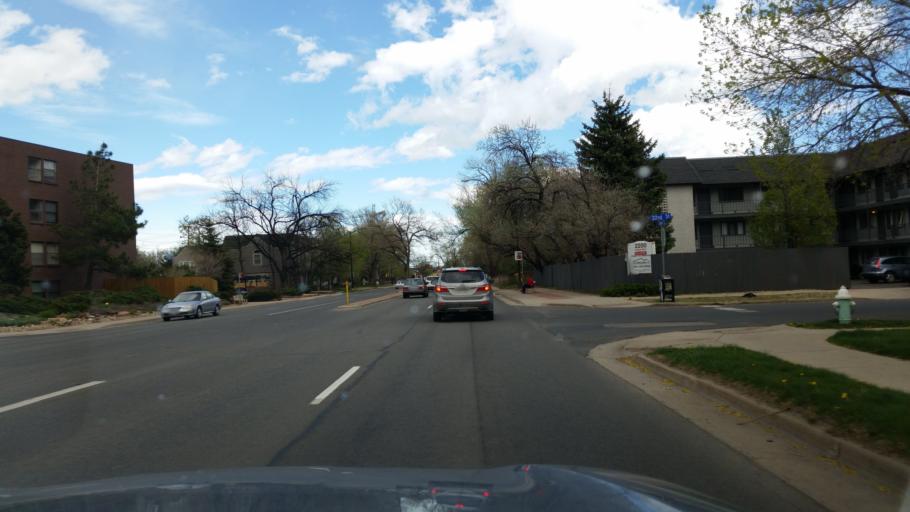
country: US
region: Colorado
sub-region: Boulder County
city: Boulder
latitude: 40.0172
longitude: -105.2666
